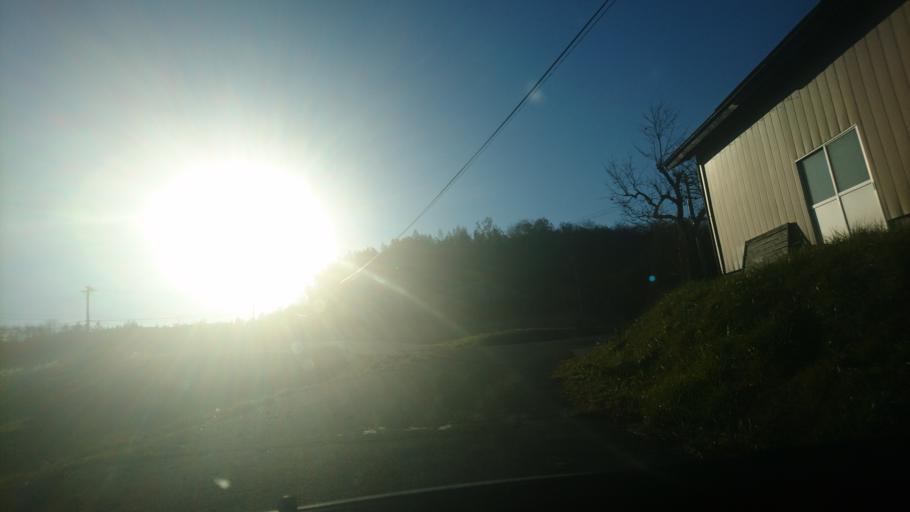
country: JP
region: Iwate
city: Ichinoseki
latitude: 38.9058
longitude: 141.1659
